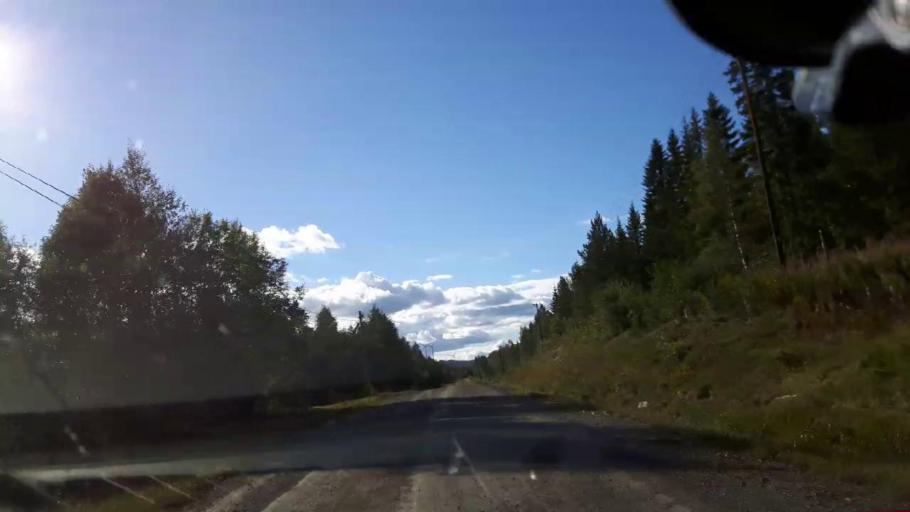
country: SE
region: Jaemtland
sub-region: Ragunda Kommun
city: Hammarstrand
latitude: 63.4886
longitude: 16.0751
